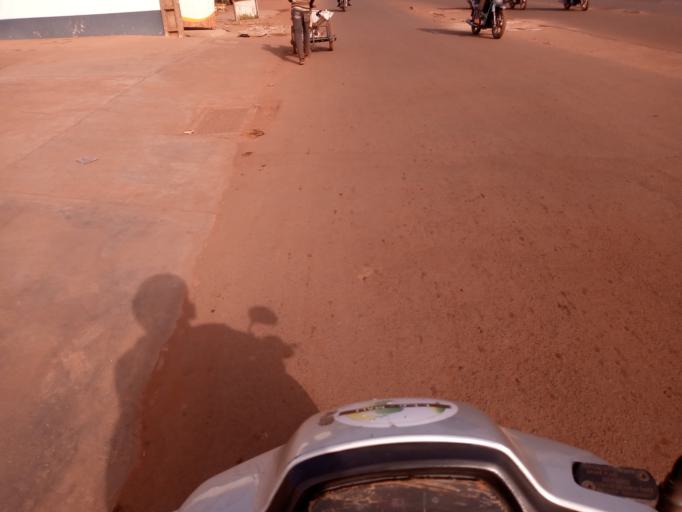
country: ML
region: Bamako
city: Bamako
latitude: 12.6045
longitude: -7.9701
